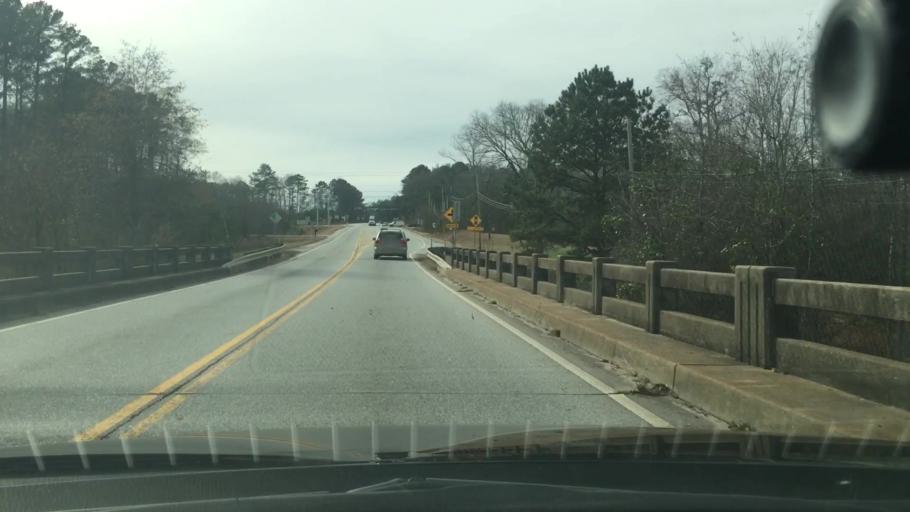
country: US
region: Georgia
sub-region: Coweta County
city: Senoia
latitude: 33.3281
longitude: -84.5091
